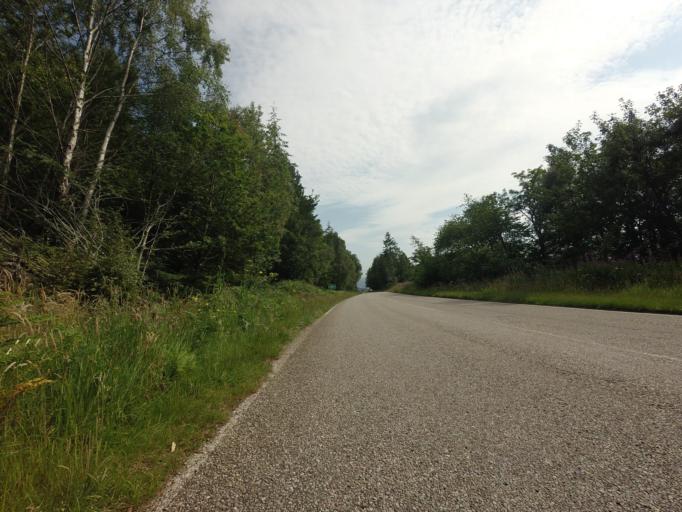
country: GB
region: Scotland
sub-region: Highland
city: Alness
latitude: 57.9067
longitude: -4.3610
